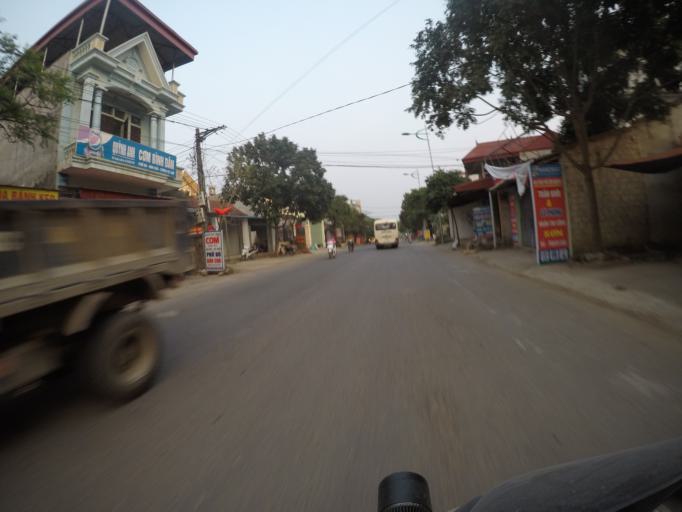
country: VN
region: Vinh Phuc
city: Trai Ngau
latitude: 21.4246
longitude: 105.5948
